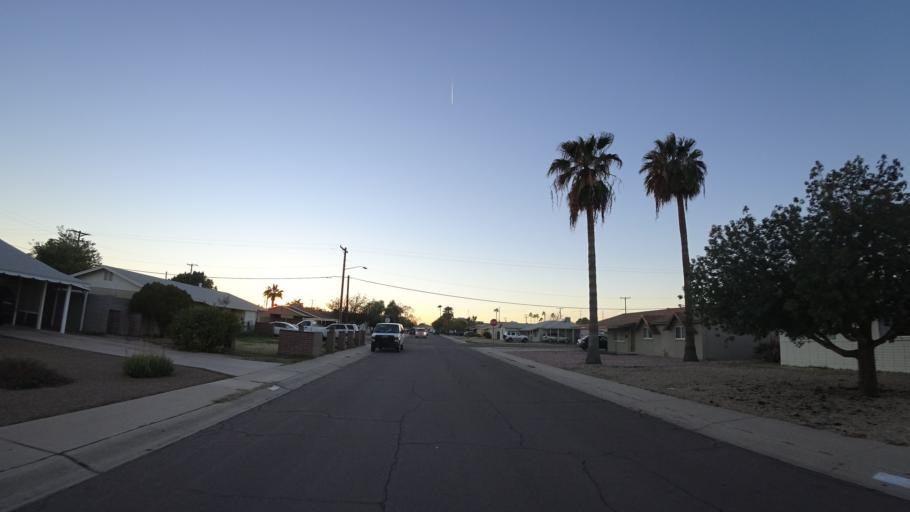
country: US
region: Arizona
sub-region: Maricopa County
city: Tempe Junction
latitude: 33.4203
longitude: -111.9581
